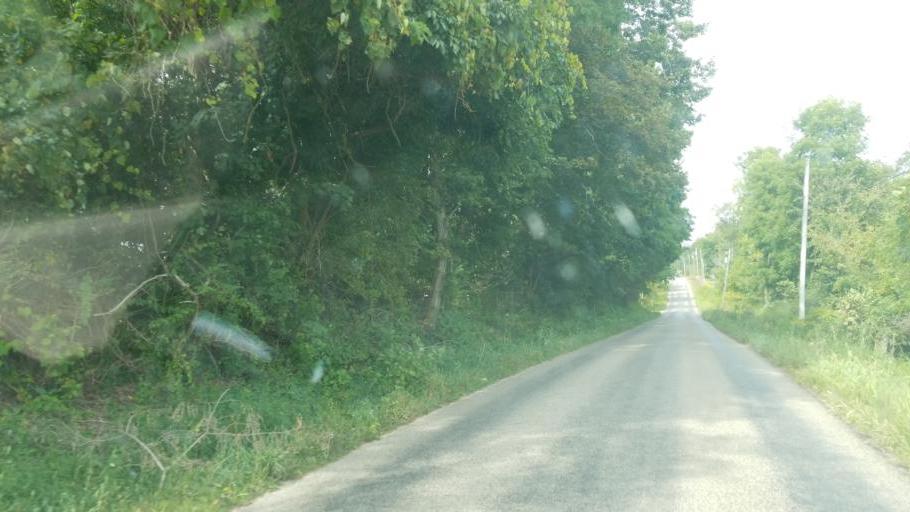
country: US
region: Ohio
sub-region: Knox County
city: Centerburg
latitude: 40.3532
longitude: -82.6068
